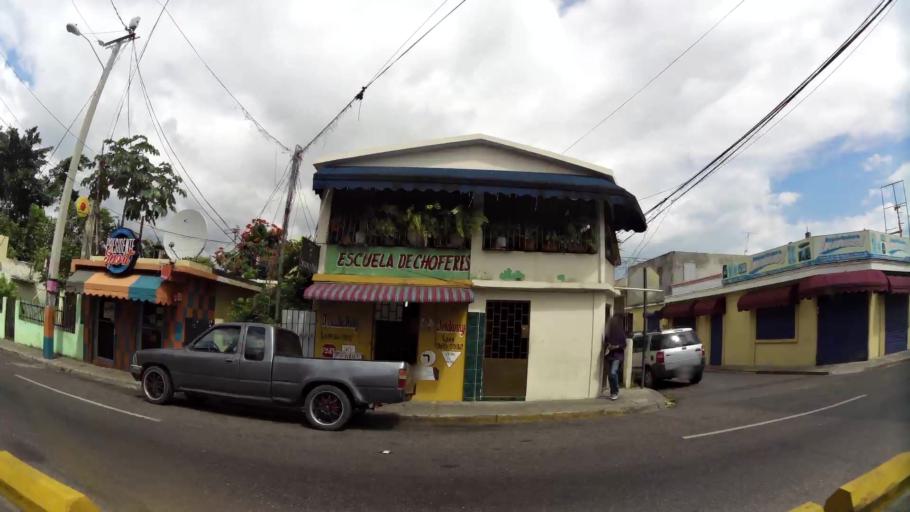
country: DO
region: Nacional
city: La Agustina
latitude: 18.4923
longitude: -69.9299
